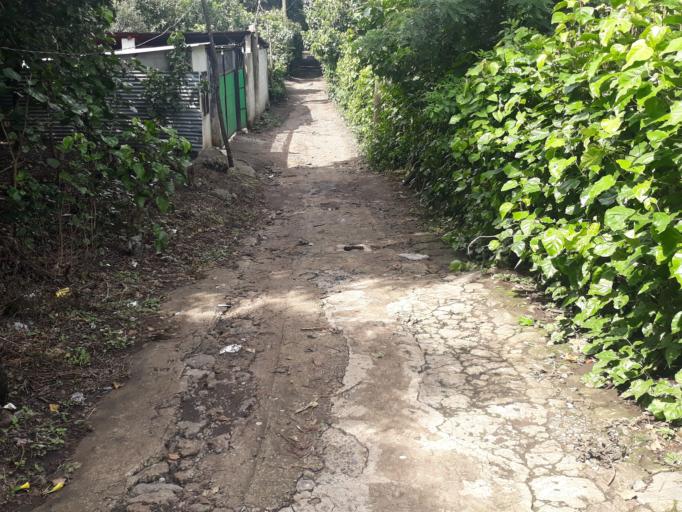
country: GT
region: Escuintla
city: San Vicente Pacaya
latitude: 14.3697
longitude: -90.5563
